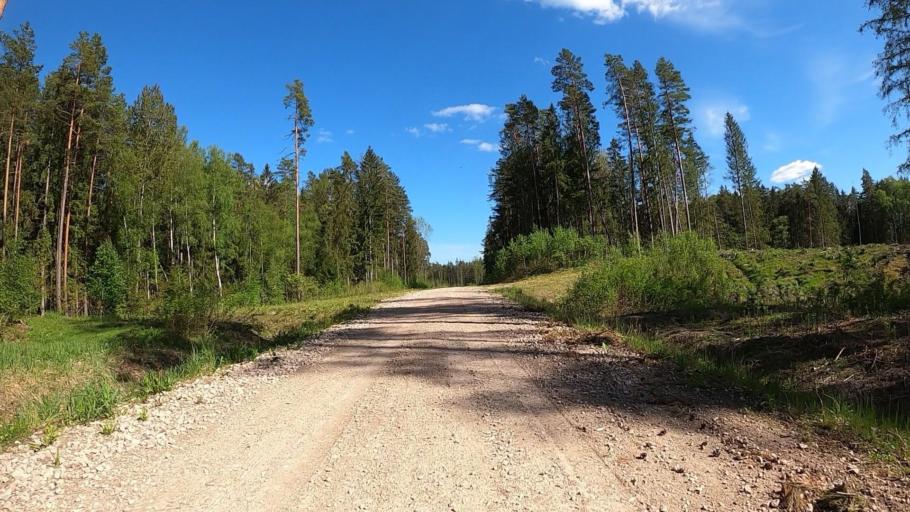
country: LV
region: Salaspils
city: Salaspils
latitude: 56.7910
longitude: 24.3341
